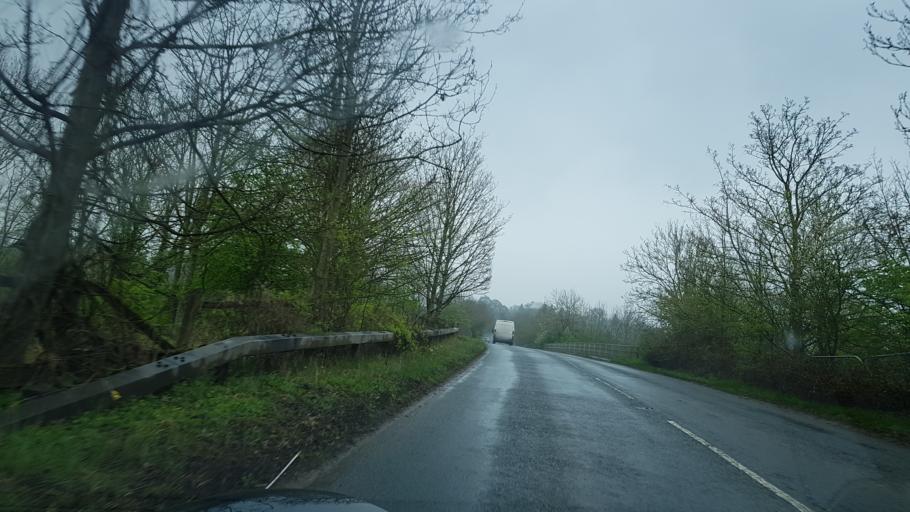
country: GB
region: England
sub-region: Herefordshire
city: Donnington
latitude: 51.9671
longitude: -2.4264
